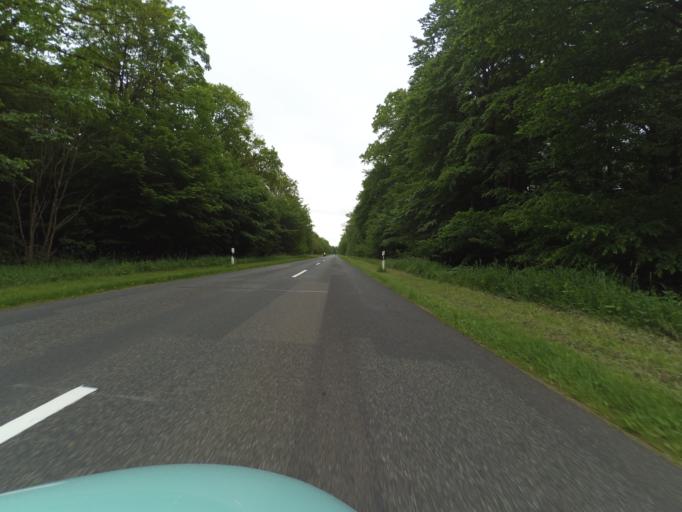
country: DE
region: Lower Saxony
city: Ribbesbuttel
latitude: 52.4057
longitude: 10.4924
